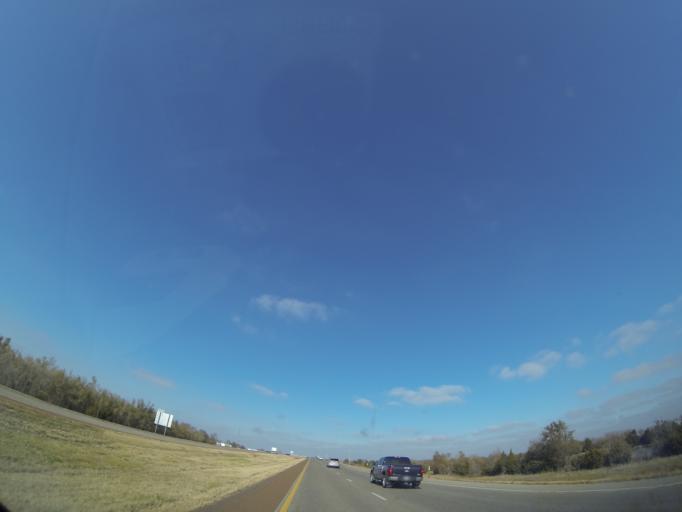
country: US
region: Kansas
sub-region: McPherson County
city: McPherson
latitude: 38.3749
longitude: -97.6205
